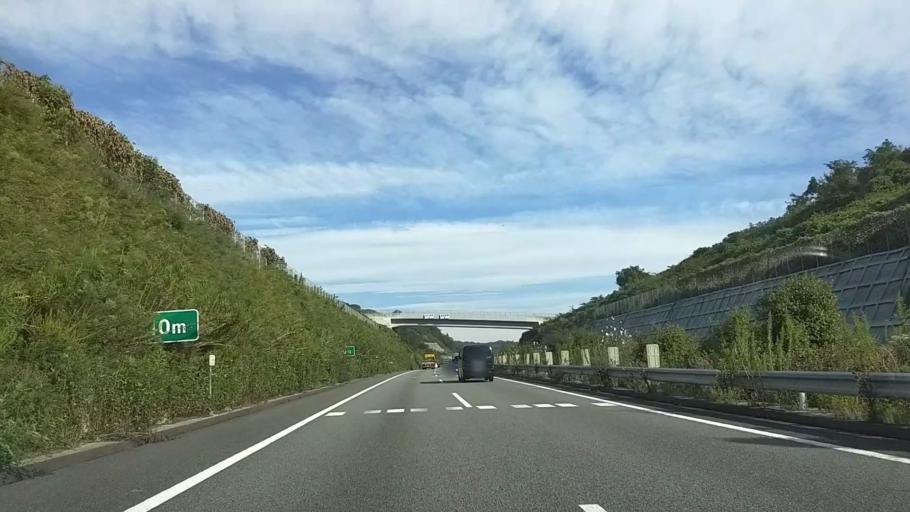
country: JP
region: Kanagawa
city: Zama
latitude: 35.5421
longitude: 139.3216
